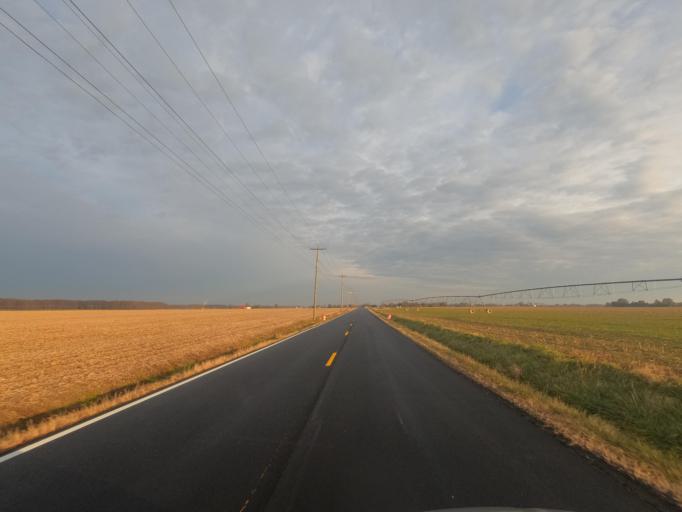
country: US
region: Delaware
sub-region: New Castle County
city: Townsend
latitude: 39.2966
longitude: -75.8307
